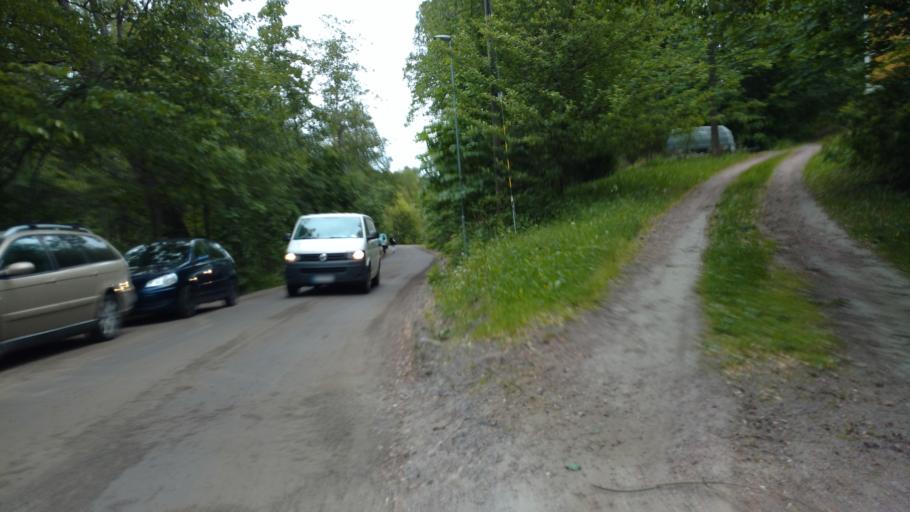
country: FI
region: Uusimaa
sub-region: Raaseporin
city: Pohja
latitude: 60.1301
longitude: 23.5457
